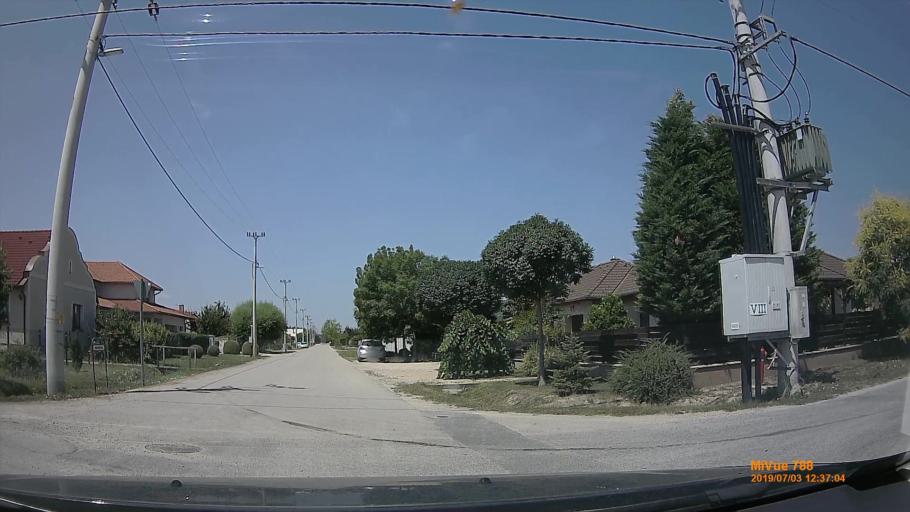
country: HU
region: Gyor-Moson-Sopron
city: Gyor
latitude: 47.7153
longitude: 17.6062
